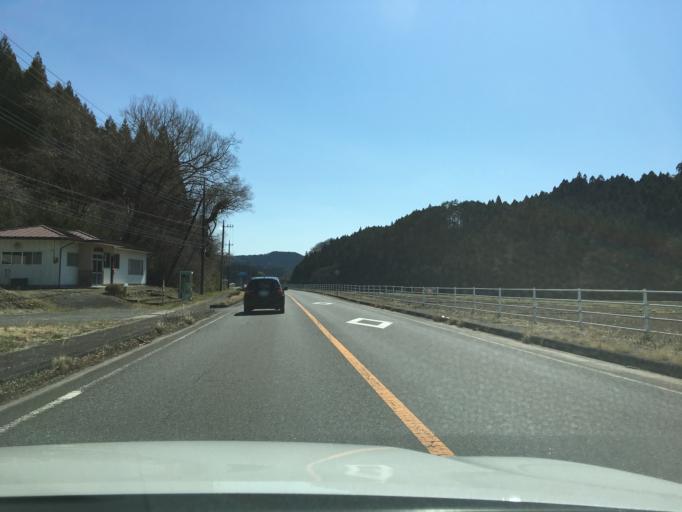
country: JP
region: Tochigi
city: Kuroiso
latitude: 37.0256
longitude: 140.1770
